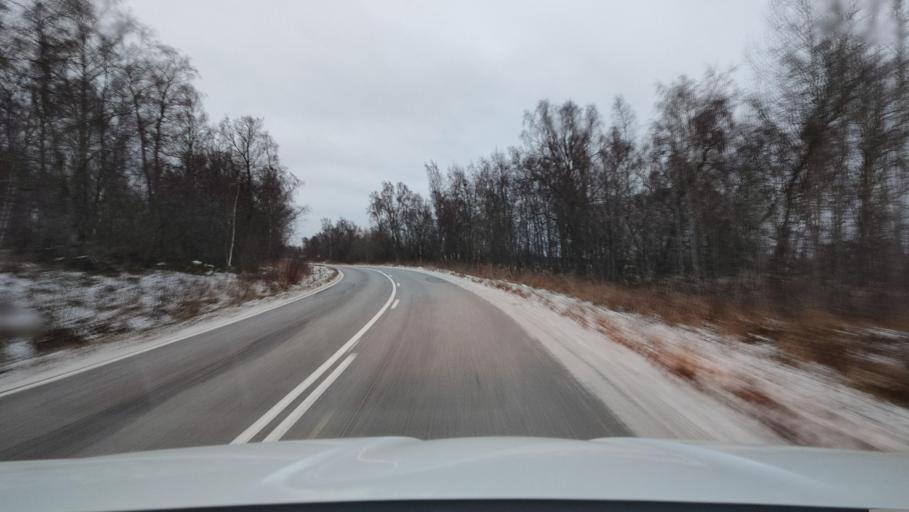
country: FI
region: Ostrobothnia
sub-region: Vaasa
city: Replot
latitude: 63.2859
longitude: 21.3329
